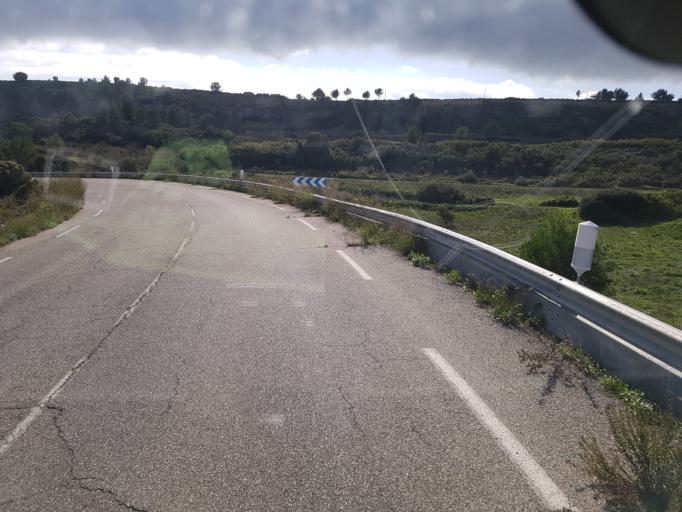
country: FR
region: Provence-Alpes-Cote d'Azur
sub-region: Departement des Bouches-du-Rhone
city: Le Rove
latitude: 43.3563
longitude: 5.2301
